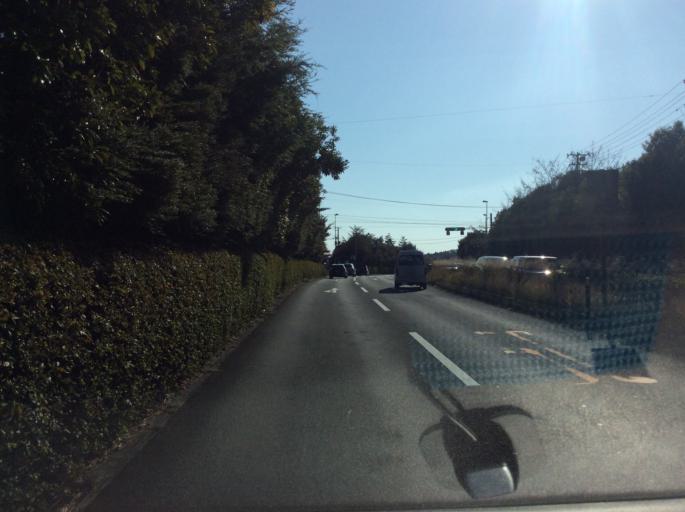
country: JP
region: Fukushima
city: Iwaki
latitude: 37.0283
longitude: 140.9027
